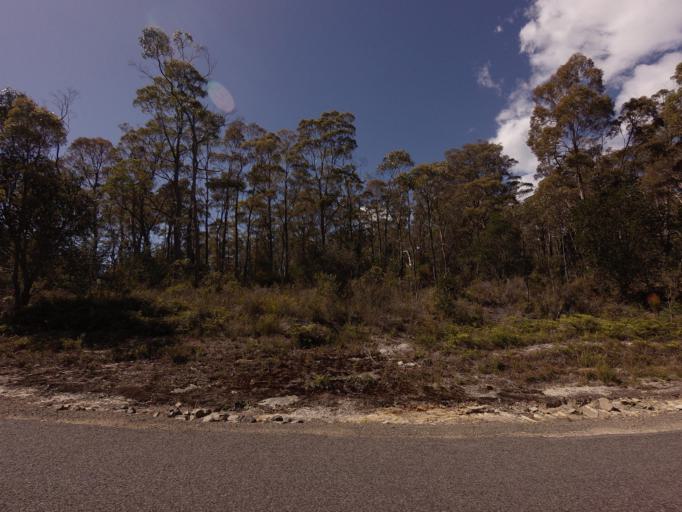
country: AU
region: Tasmania
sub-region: Break O'Day
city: St Helens
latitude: -41.6086
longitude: 148.2124
